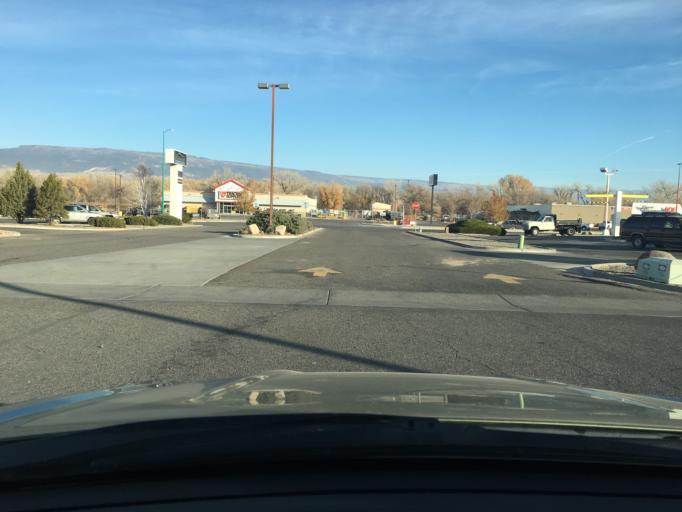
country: US
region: Colorado
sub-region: Delta County
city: Delta
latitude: 38.7481
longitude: -108.0719
